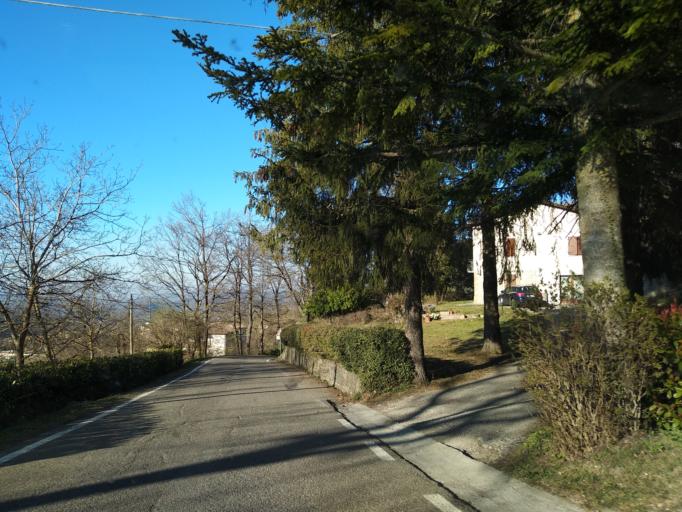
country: IT
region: Emilia-Romagna
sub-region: Provincia di Reggio Emilia
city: Castelnovo ne'Monti
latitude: 44.4241
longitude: 10.4080
